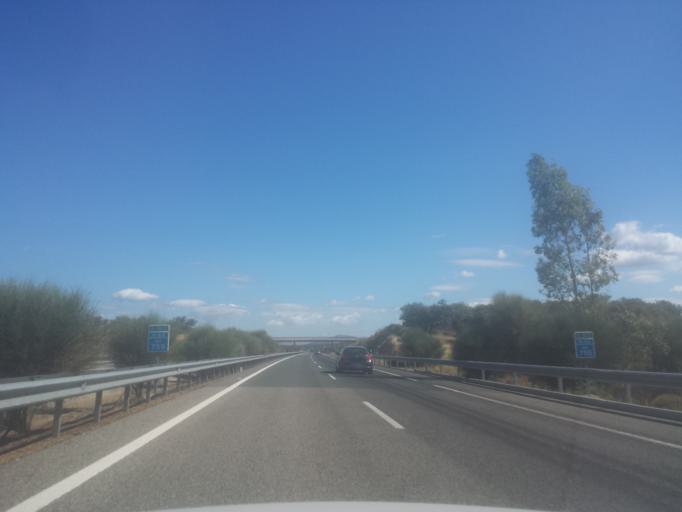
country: ES
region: Andalusia
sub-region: Provincia de Huelva
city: Santa Olalla del Cala
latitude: 37.8397
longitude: -6.2201
